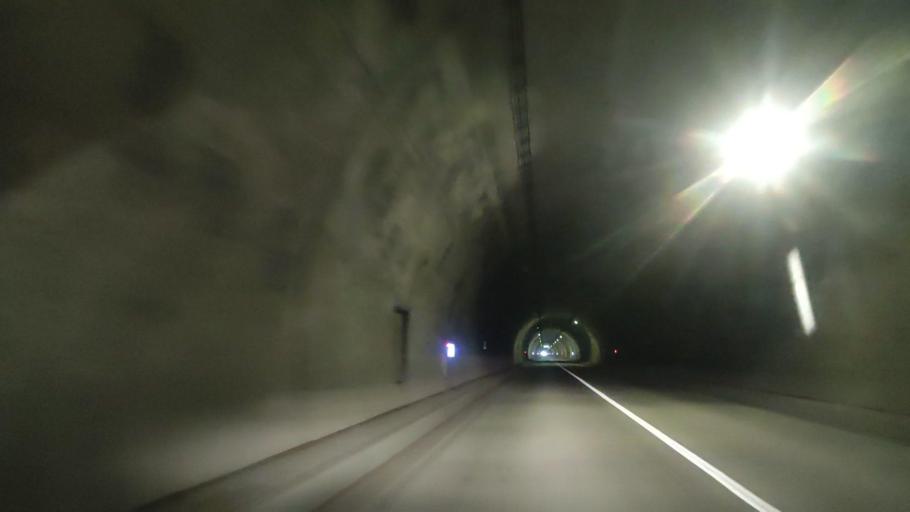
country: JP
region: Hokkaido
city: Iwamizawa
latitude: 43.0266
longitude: 142.0873
